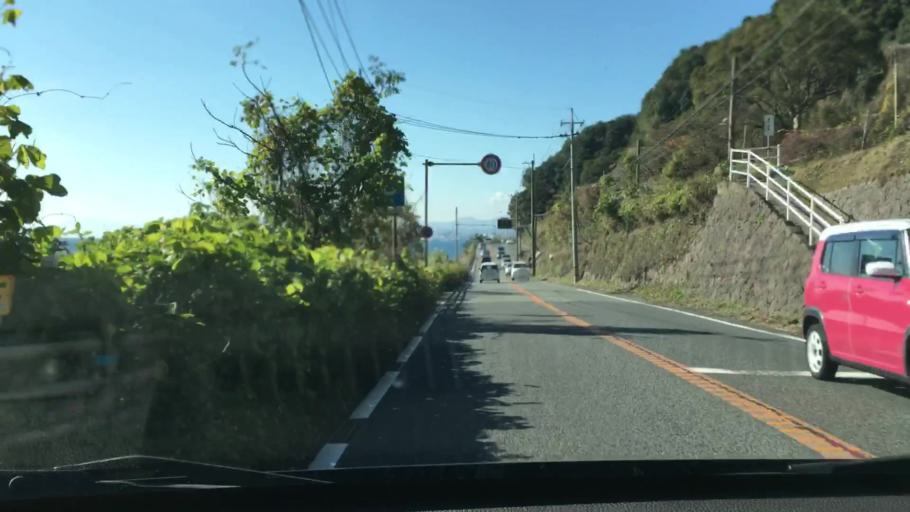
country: JP
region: Kagoshima
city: Kagoshima-shi
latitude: 31.6280
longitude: 130.5969
